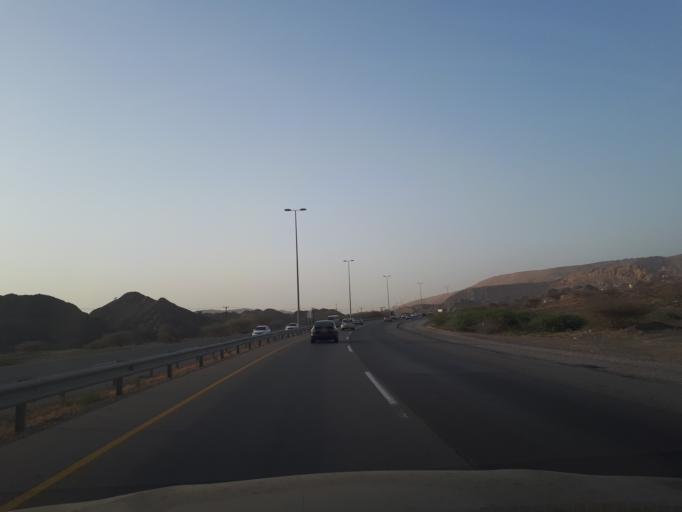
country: OM
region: Muhafazat ad Dakhiliyah
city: Bidbid
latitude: 23.5136
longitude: 58.1916
